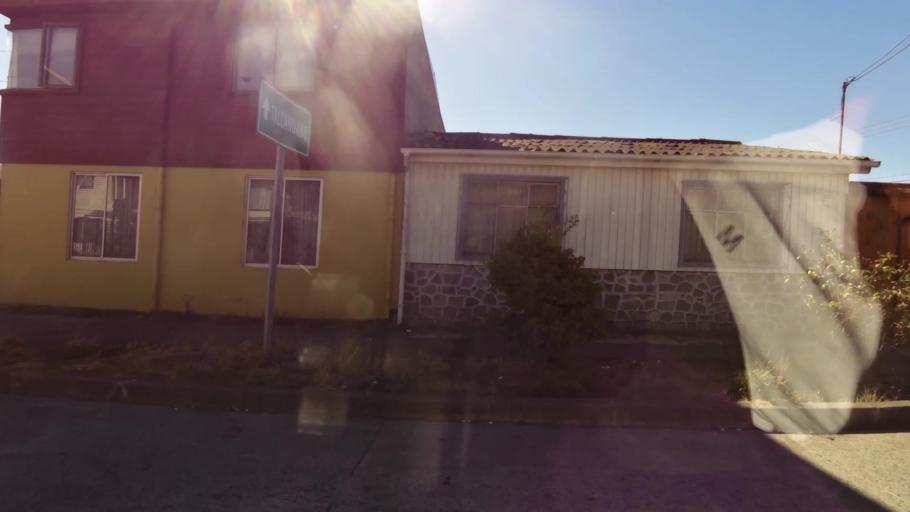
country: CL
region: Biobio
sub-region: Provincia de Concepcion
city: Concepcion
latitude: -36.8111
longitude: -73.0735
